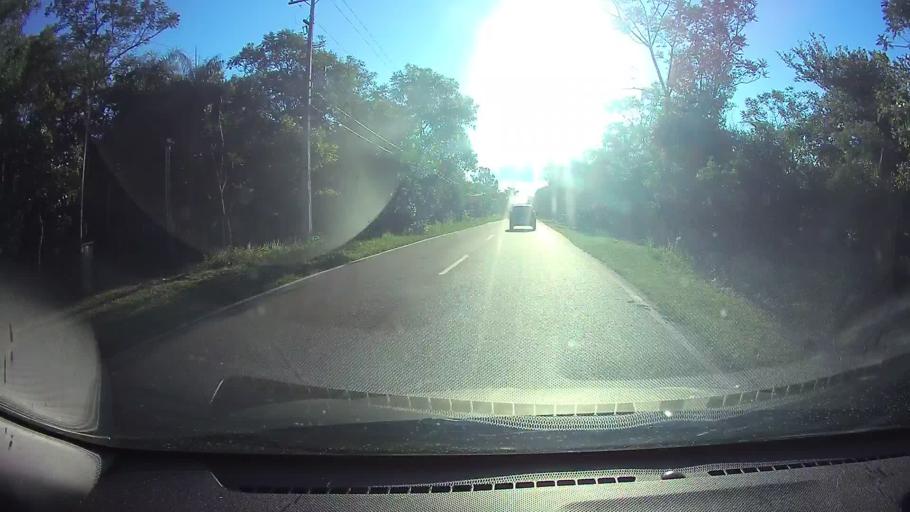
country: PY
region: Cordillera
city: Emboscada
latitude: -25.2030
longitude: -57.3357
